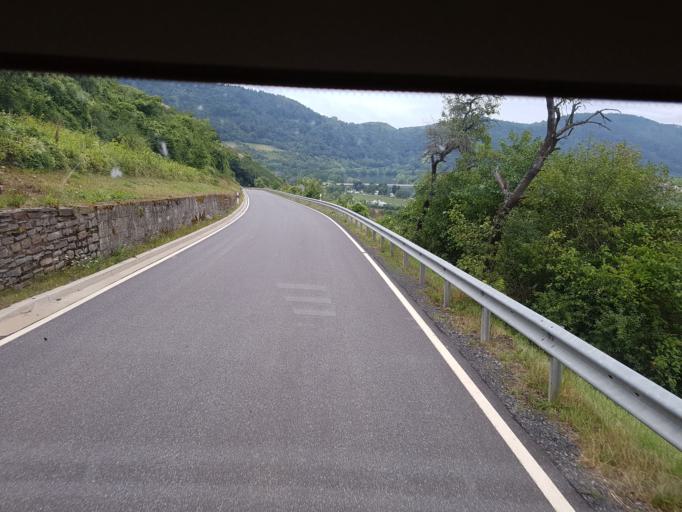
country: DE
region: Rheinland-Pfalz
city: Senheim
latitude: 50.0872
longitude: 7.2164
